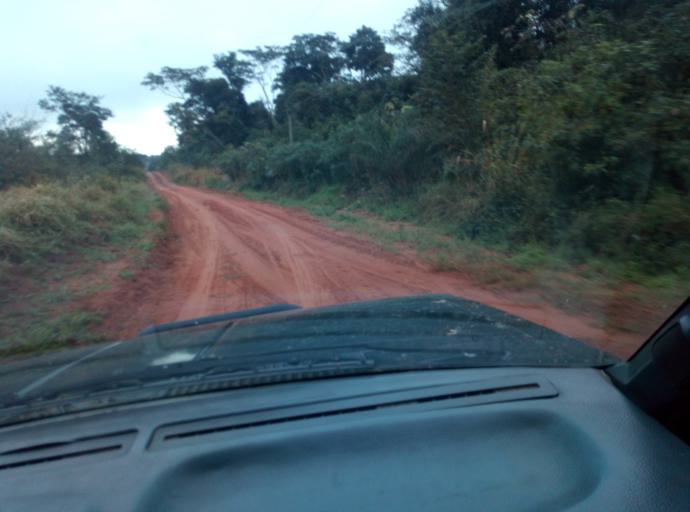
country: PY
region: Caaguazu
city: Carayao
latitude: -25.1904
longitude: -56.3451
